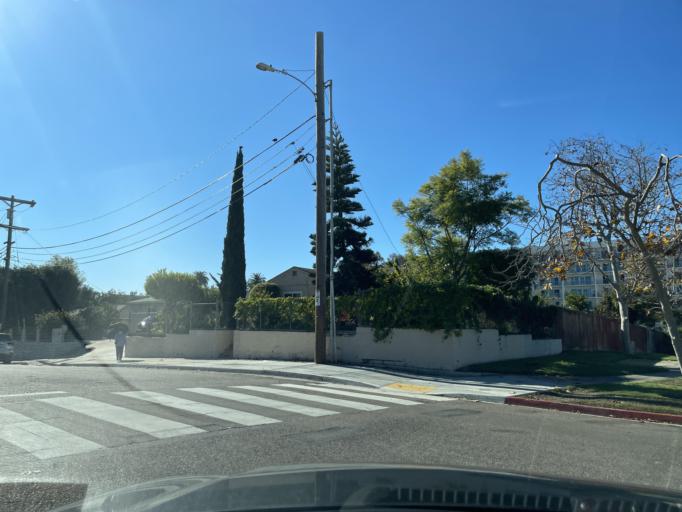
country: US
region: California
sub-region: San Diego County
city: National City
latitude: 32.6724
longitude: -117.0987
